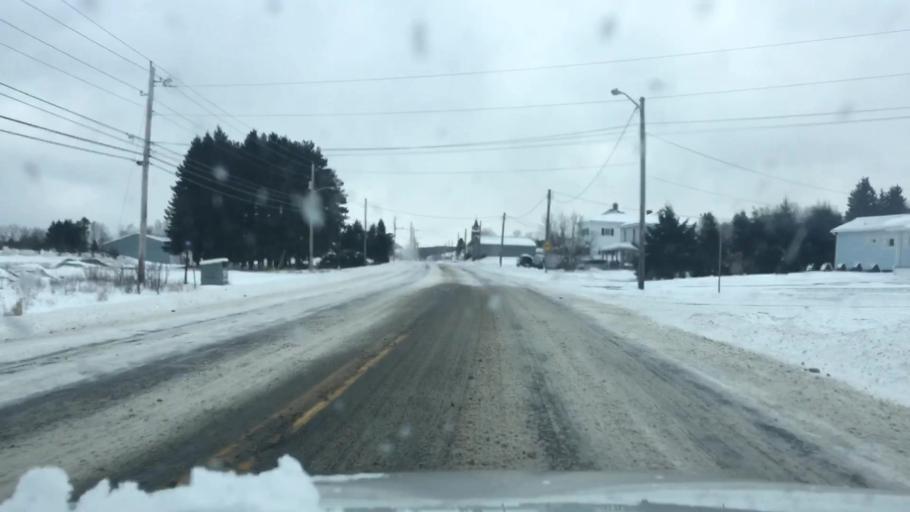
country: US
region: Maine
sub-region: Aroostook County
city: Madawaska
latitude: 47.3119
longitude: -68.1594
